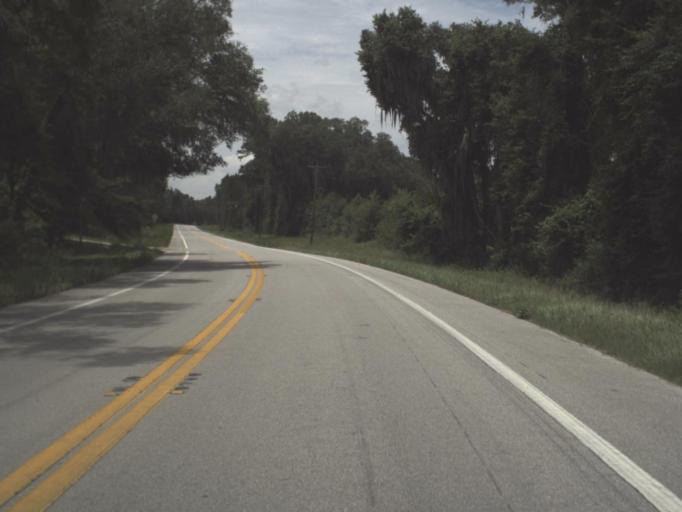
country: US
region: Florida
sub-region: Madison County
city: Madison
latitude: 30.5505
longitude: -83.4261
